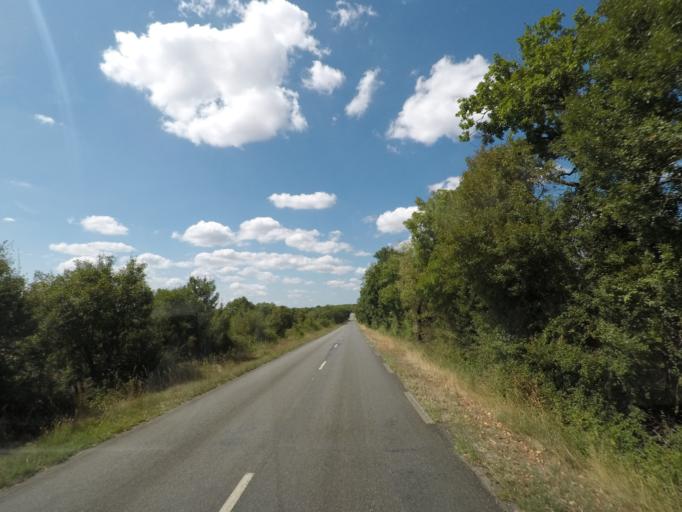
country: FR
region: Midi-Pyrenees
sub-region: Departement du Lot
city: Lacapelle-Marival
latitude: 44.6268
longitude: 1.8437
